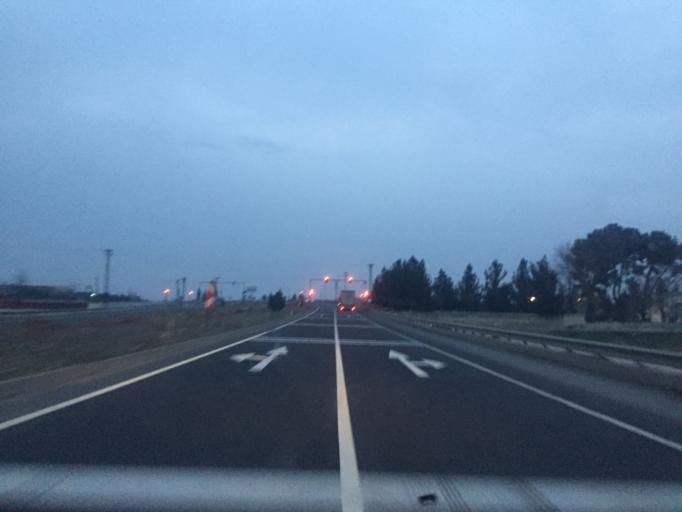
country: TR
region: Sanliurfa
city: Camlidere
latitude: 37.1536
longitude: 39.0673
